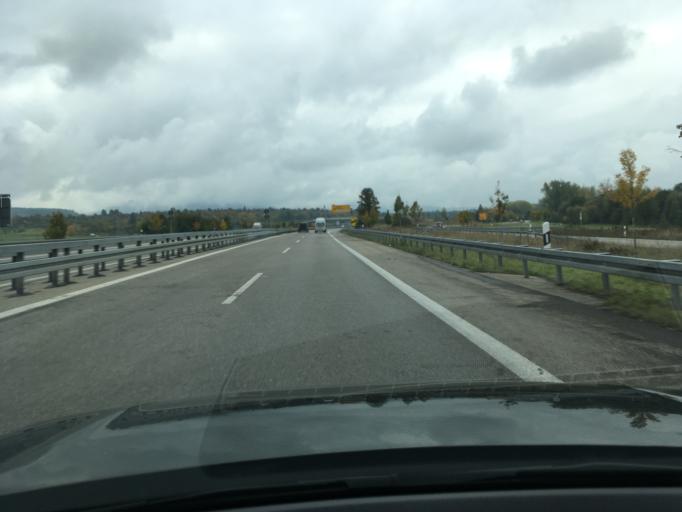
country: DE
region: Baden-Wuerttemberg
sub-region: Tuebingen Region
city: Dusslingen
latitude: 48.4434
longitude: 9.0577
